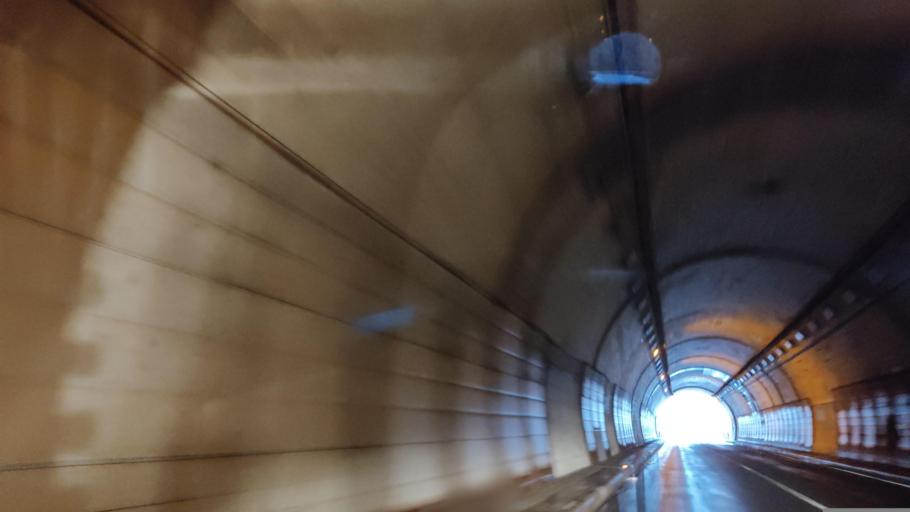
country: JP
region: Iwate
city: Shizukuishi
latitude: 39.7015
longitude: 140.7633
